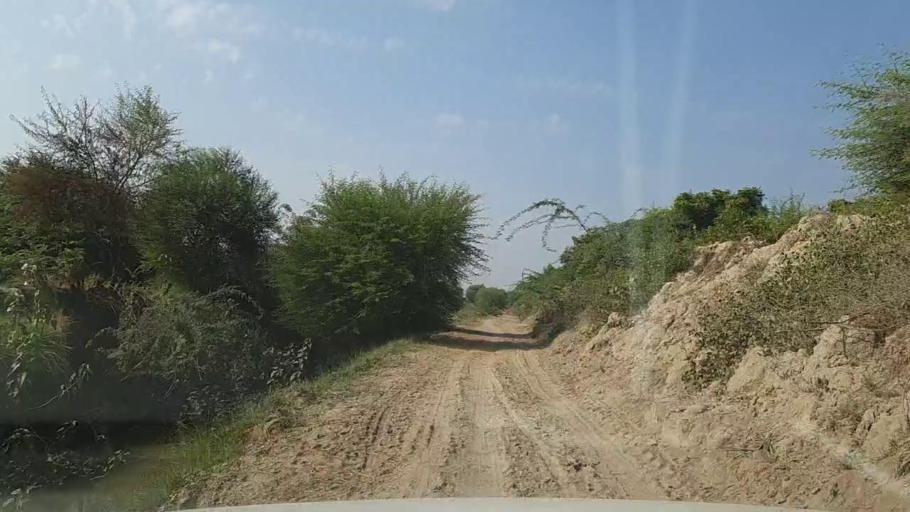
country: PK
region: Sindh
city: Mirpur Batoro
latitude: 24.7092
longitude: 68.2987
